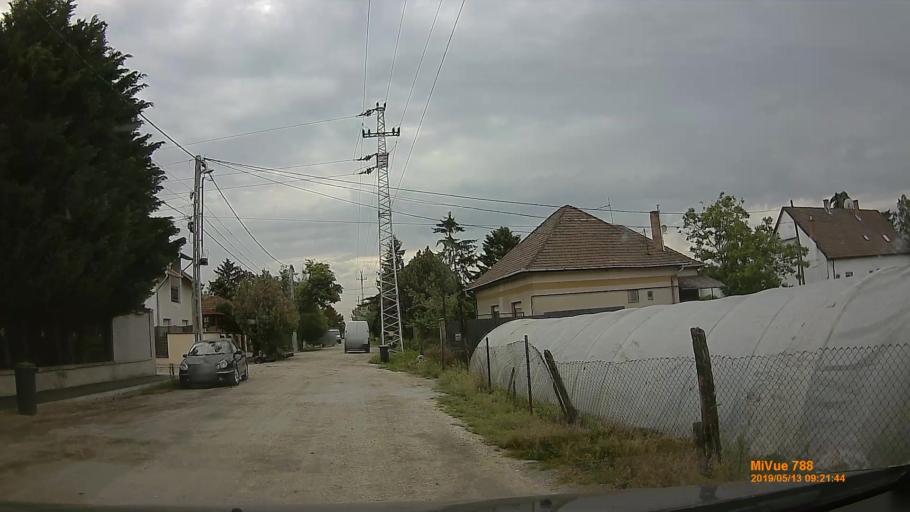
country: HU
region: Budapest
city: Budapest XXIII. keruelet
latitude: 47.3991
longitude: 19.0874
